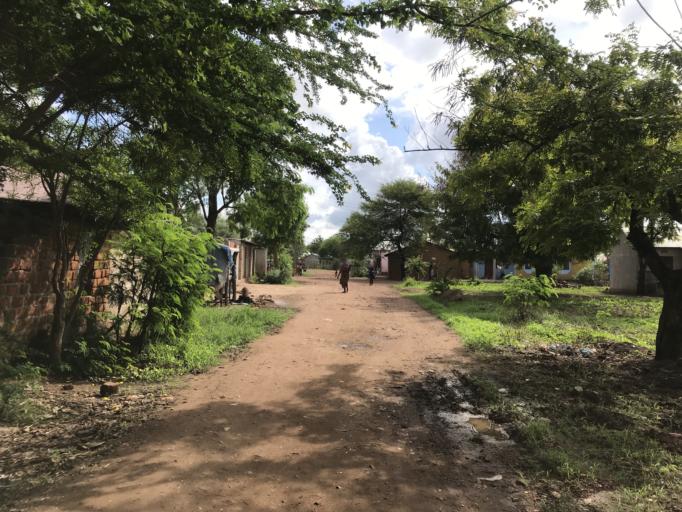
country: TZ
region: Tabora
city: Igunga
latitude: -4.2890
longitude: 33.8818
